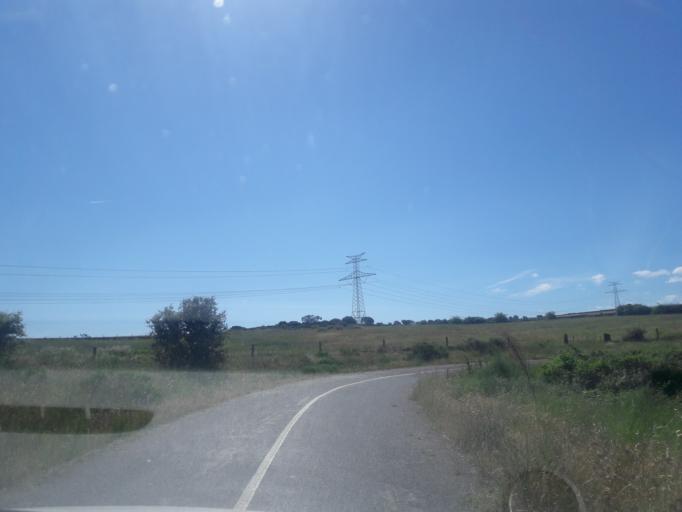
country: ES
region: Castille and Leon
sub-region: Provincia de Salamanca
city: Lumbrales
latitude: 40.9904
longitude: -6.7304
